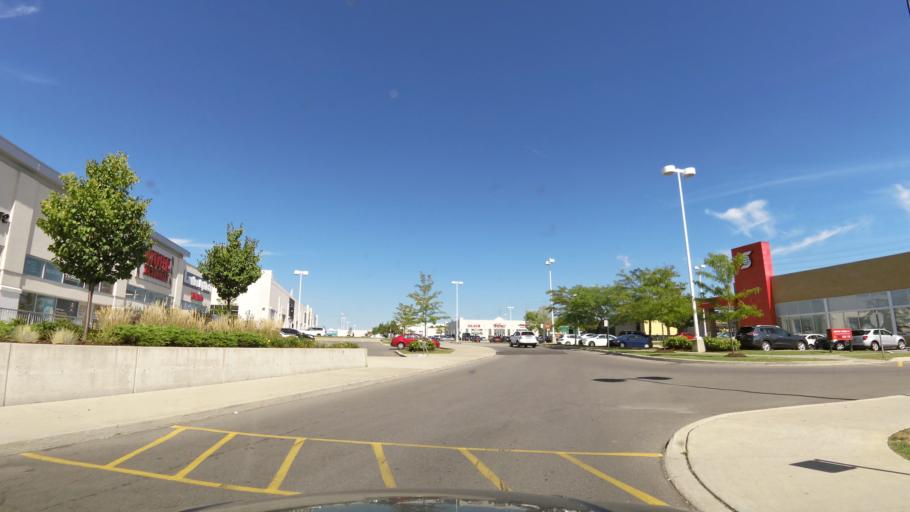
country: CA
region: Ontario
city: Mississauga
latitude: 43.6094
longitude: -79.7006
